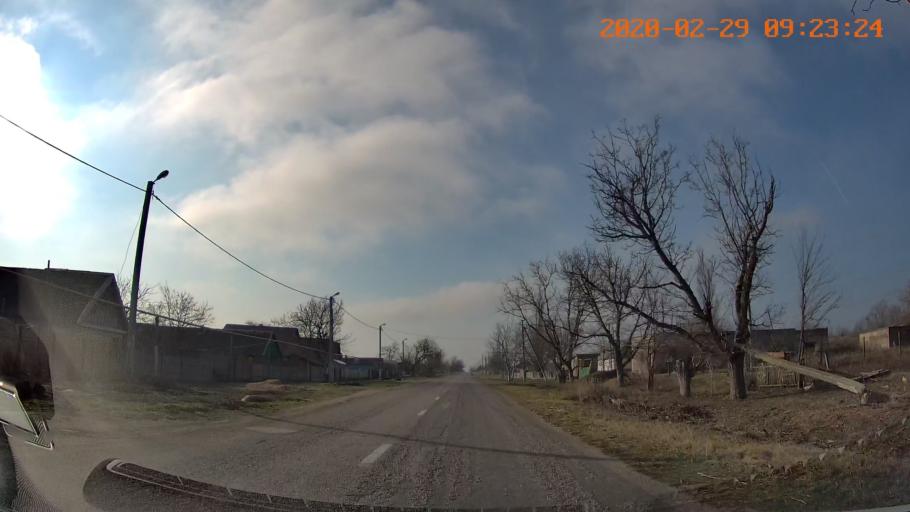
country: MD
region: Telenesti
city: Pervomaisc
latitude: 46.7262
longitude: 29.9613
